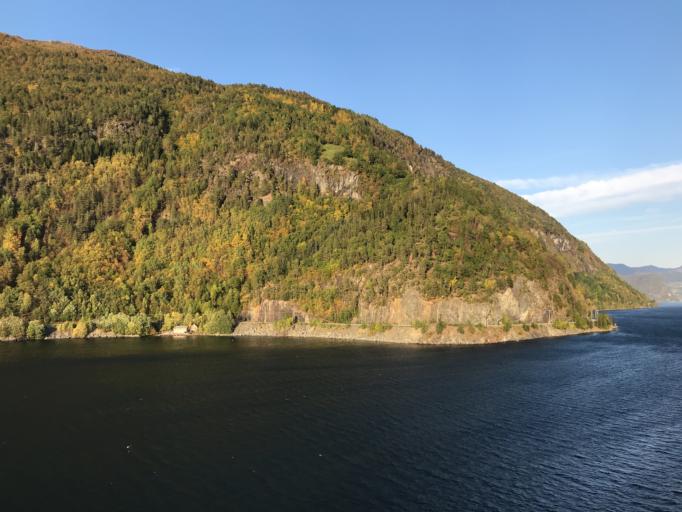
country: NO
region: Sogn og Fjordane
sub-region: Gloppen
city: Sandane
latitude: 61.8449
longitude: 6.1293
